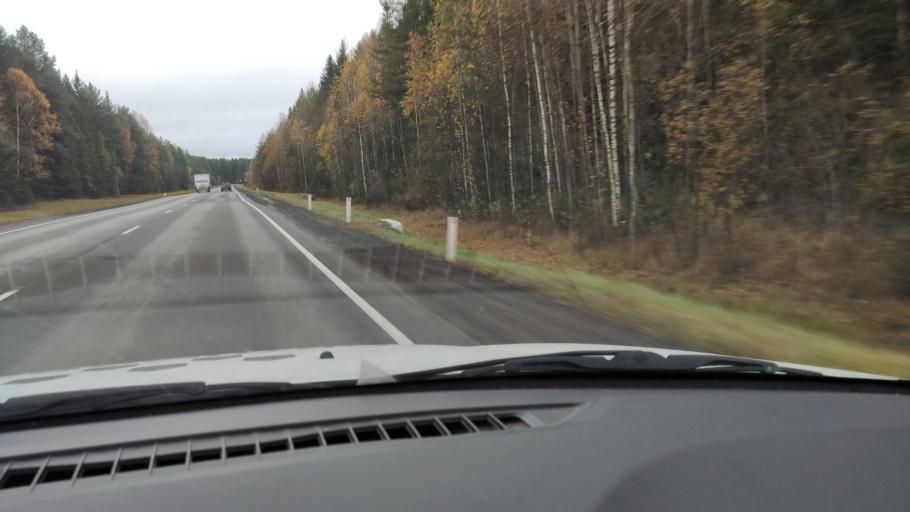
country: RU
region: Kirov
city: Belaya Kholunitsa
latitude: 58.8833
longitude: 50.8727
